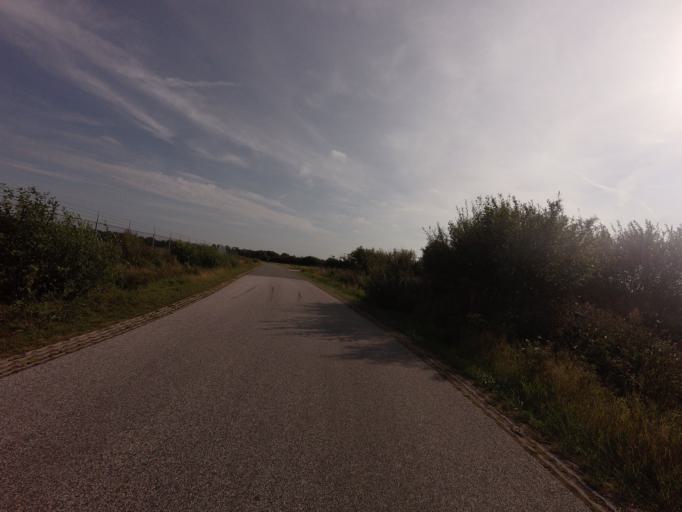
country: NL
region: Drenthe
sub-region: Gemeente Tynaarlo
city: Vries
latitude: 53.1106
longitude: 6.5556
